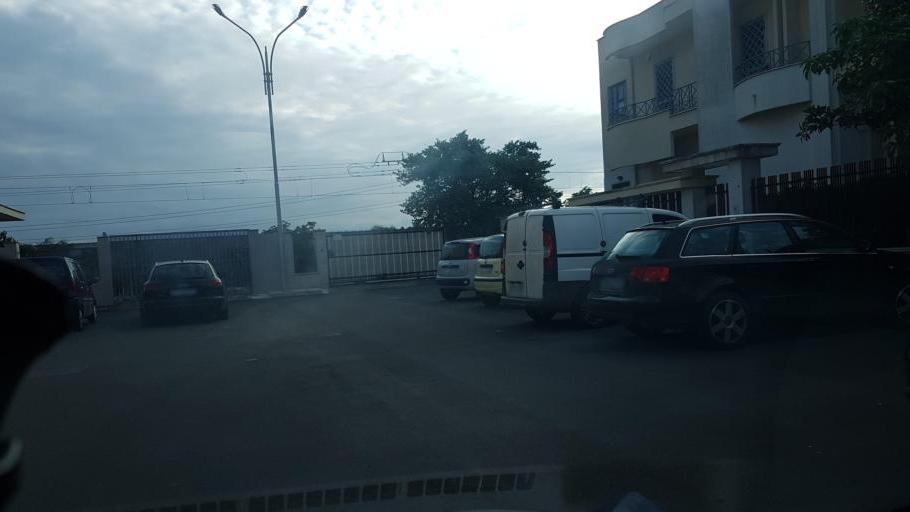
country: IT
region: Apulia
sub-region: Provincia di Brindisi
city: Francavilla Fontana
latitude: 40.5234
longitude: 17.5923
